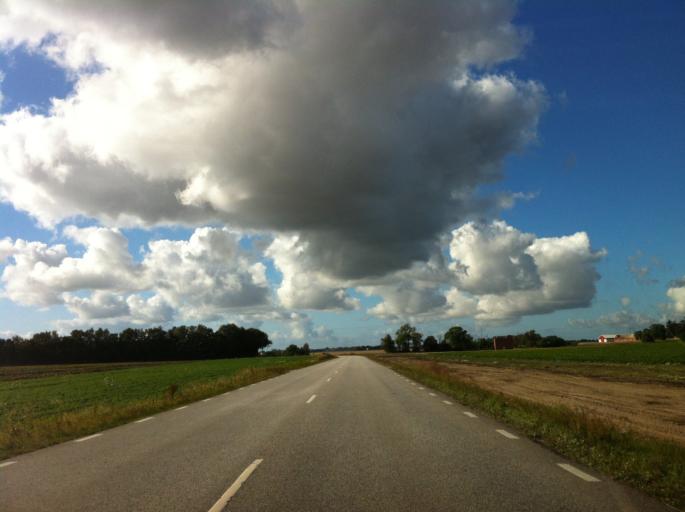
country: SE
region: Skane
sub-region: Lunds Kommun
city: Lund
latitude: 55.7907
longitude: 13.2255
